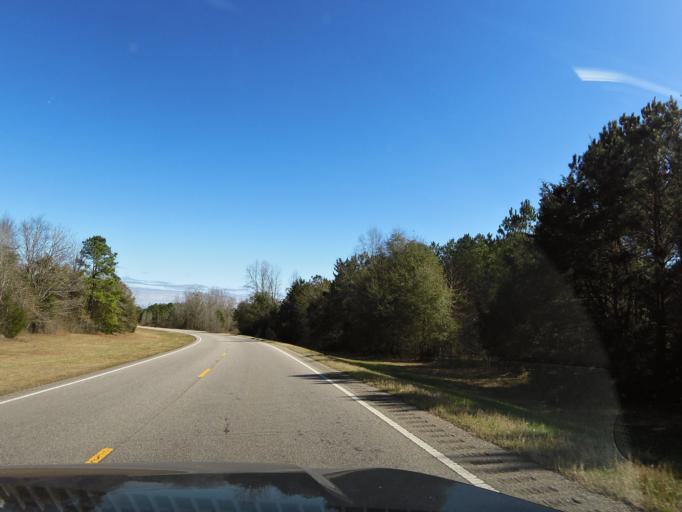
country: US
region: Alabama
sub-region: Barbour County
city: Clayton
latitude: 32.0726
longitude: -85.5060
